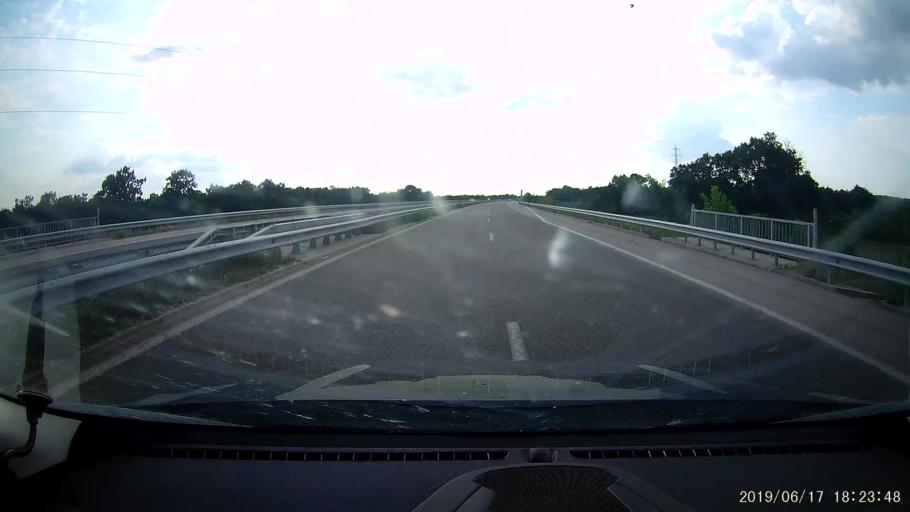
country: BG
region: Khaskovo
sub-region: Obshtina Dimitrovgrad
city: Dimitrovgrad
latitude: 41.9778
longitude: 25.7096
